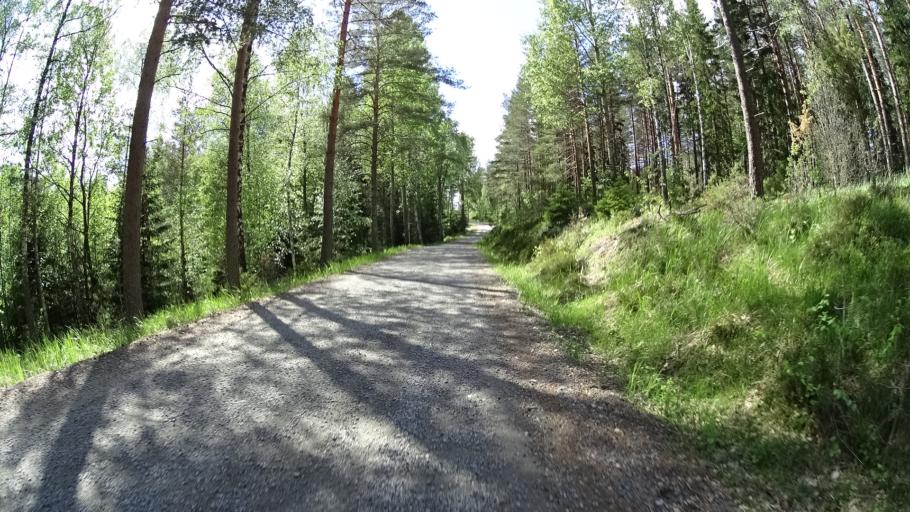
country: FI
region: Varsinais-Suomi
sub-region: Salo
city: Kisko
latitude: 60.1882
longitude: 23.5699
